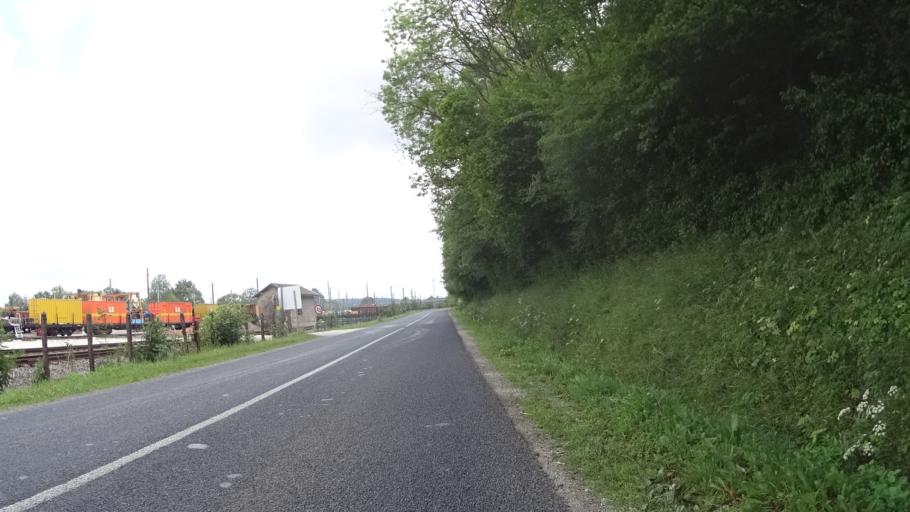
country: FR
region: Lorraine
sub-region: Departement de la Meuse
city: Lerouville
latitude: 48.7985
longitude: 5.5336
